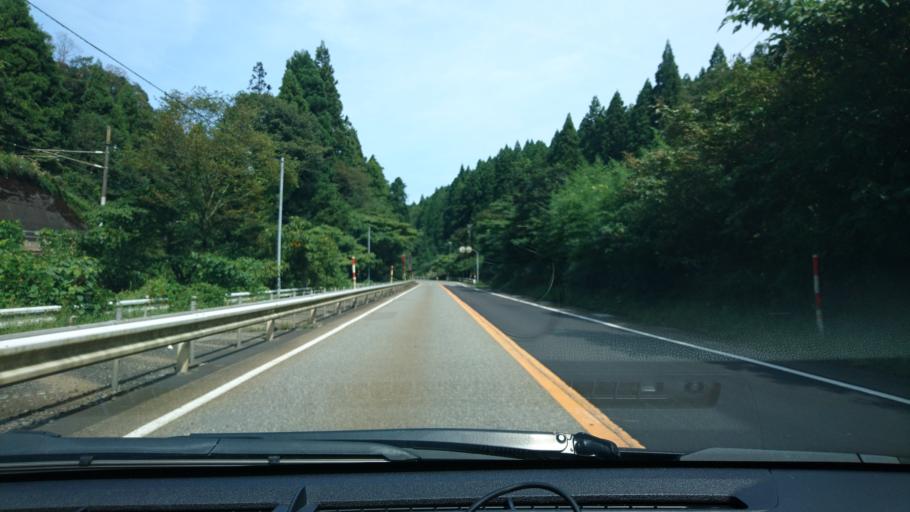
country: JP
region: Fukui
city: Maruoka
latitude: 36.2737
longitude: 136.2898
